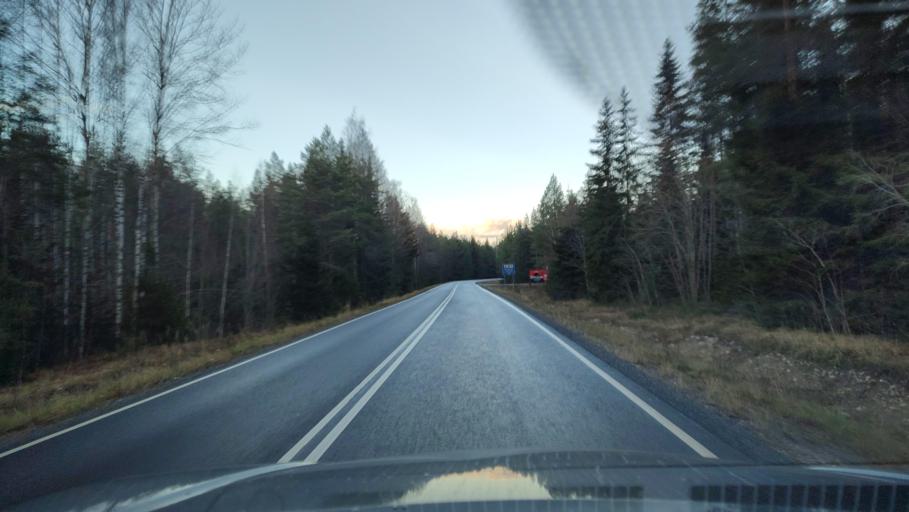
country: FI
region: Southern Ostrobothnia
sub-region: Suupohja
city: Karijoki
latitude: 62.2864
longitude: 21.6236
